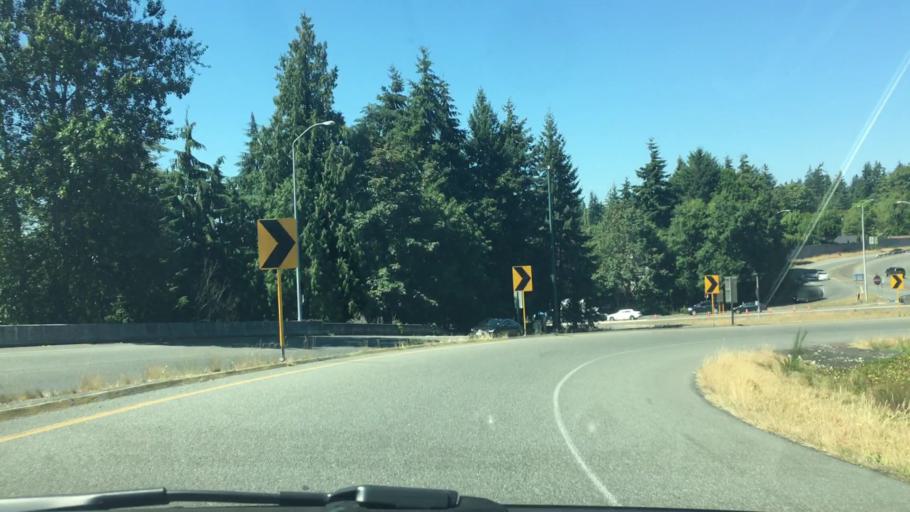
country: US
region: Washington
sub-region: King County
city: Kirkland
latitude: 47.6781
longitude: -122.1863
